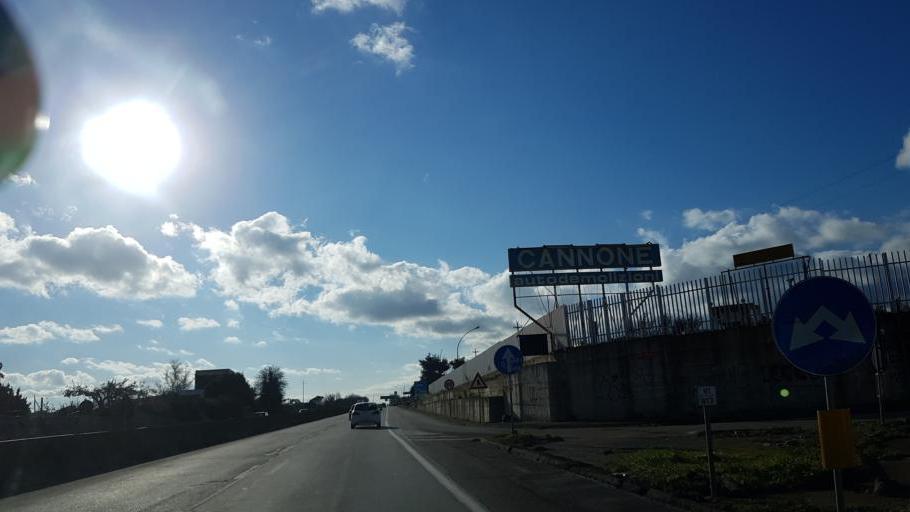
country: IT
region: Apulia
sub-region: Provincia di Brindisi
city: Brindisi
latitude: 40.6359
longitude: 17.9163
